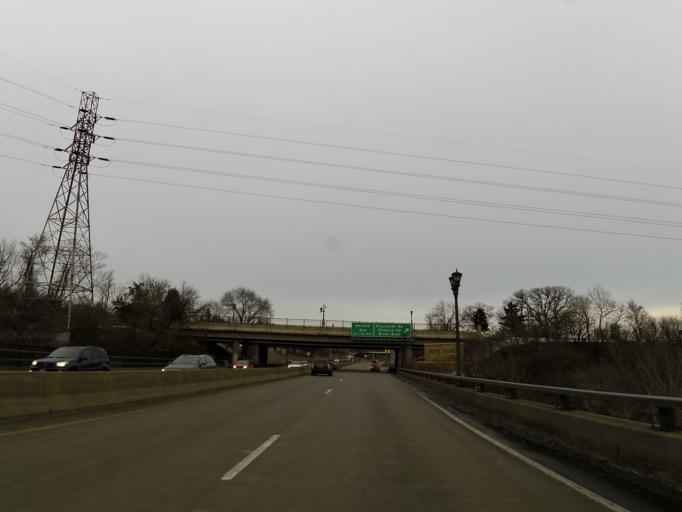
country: US
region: Minnesota
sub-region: Dakota County
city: Mendota Heights
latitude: 44.8956
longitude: -93.1803
